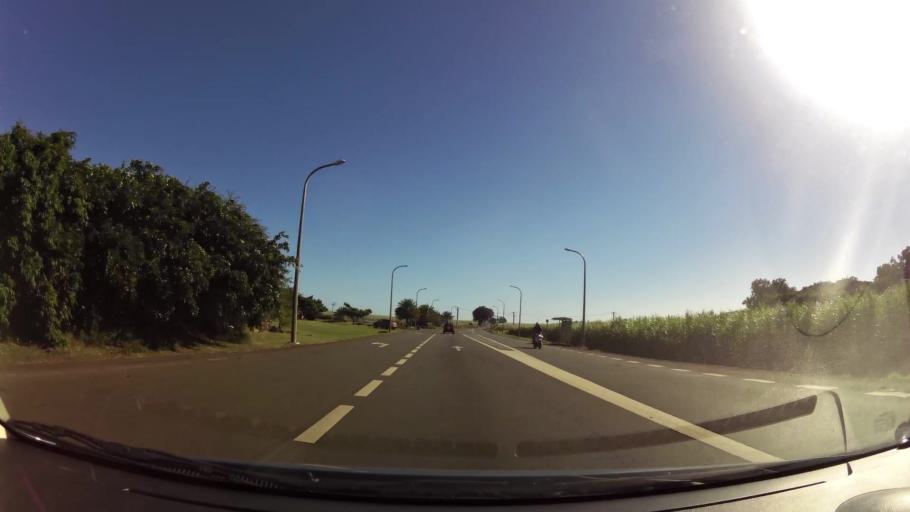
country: MU
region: Black River
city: Cascavelle
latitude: -20.3107
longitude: 57.4031
